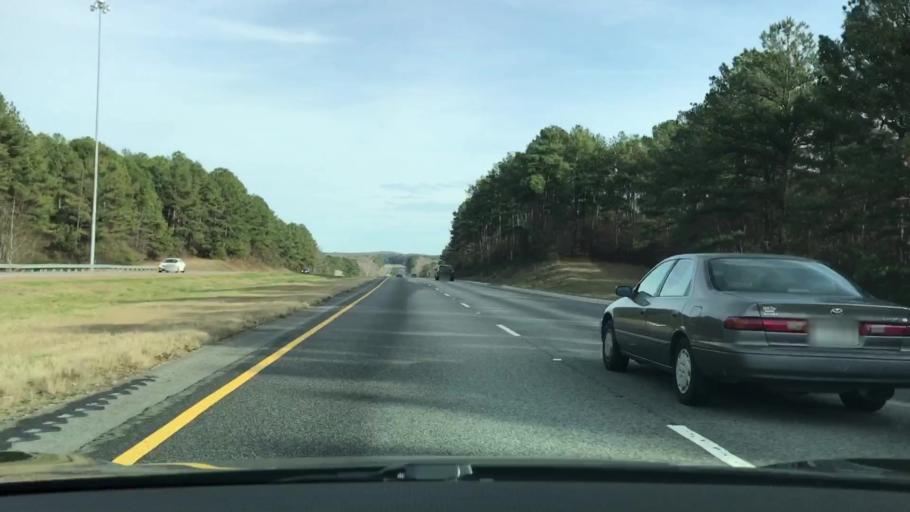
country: US
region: Georgia
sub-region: Newton County
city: Covington
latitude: 33.6117
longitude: -83.8187
